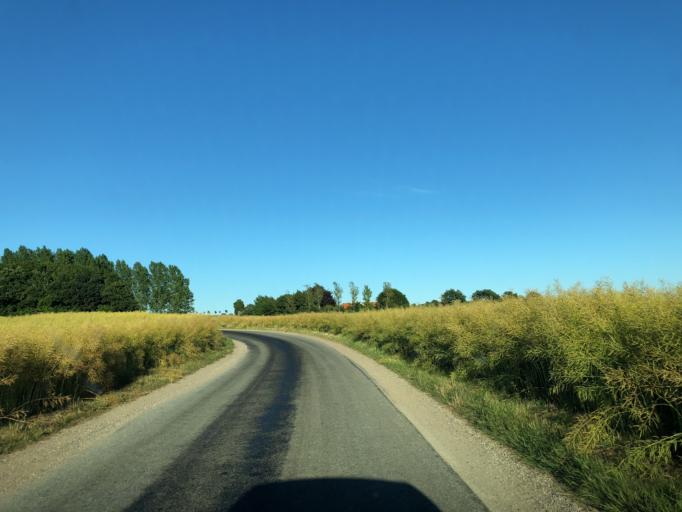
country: DK
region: Central Jutland
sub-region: Horsens Kommune
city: Horsens
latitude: 55.9234
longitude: 9.8694
